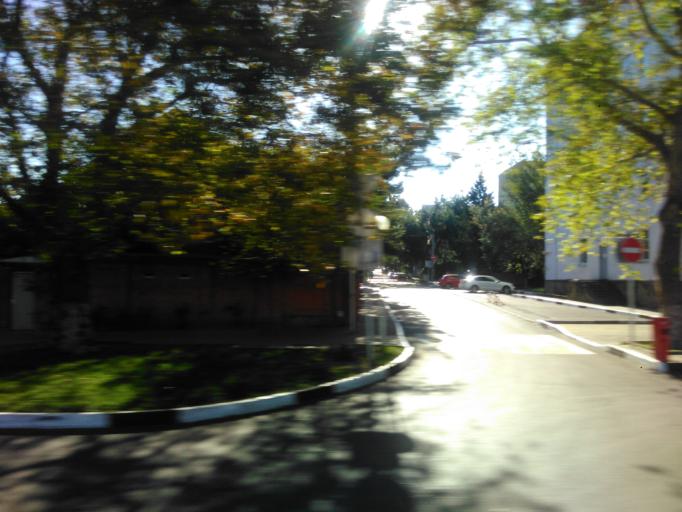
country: RU
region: Krasnodarskiy
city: Gelendzhik
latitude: 44.5553
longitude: 38.0764
